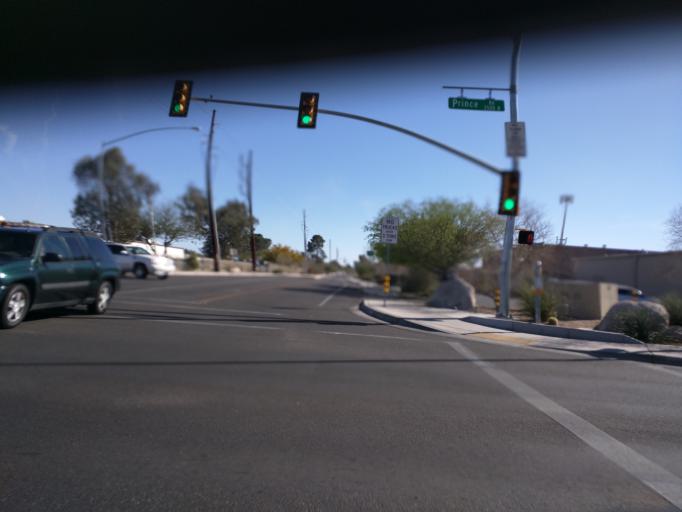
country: US
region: Arizona
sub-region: Pima County
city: Catalina Foothills
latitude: 32.2721
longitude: -110.9524
